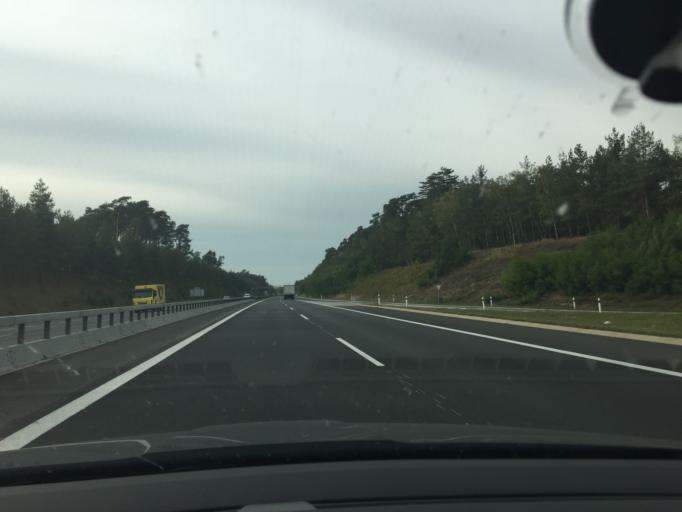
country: CZ
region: Central Bohemia
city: Poricany
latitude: 50.1193
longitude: 14.9418
